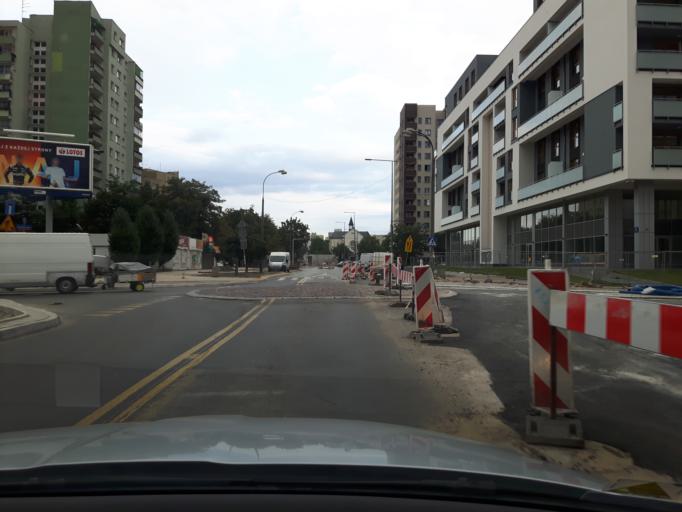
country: PL
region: Masovian Voivodeship
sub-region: Warszawa
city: Praga Polnoc
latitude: 52.2702
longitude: 21.0478
